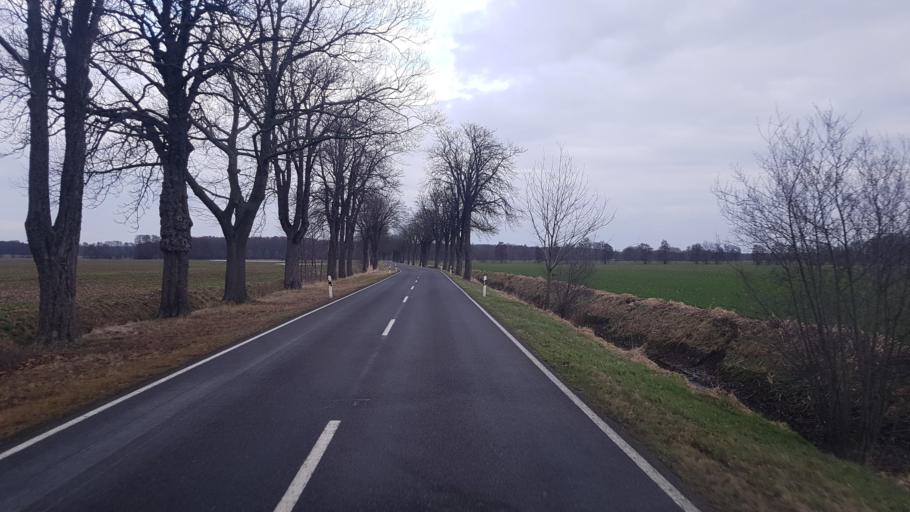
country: DE
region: Brandenburg
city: Drahnsdorf
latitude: 51.9222
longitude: 13.6048
